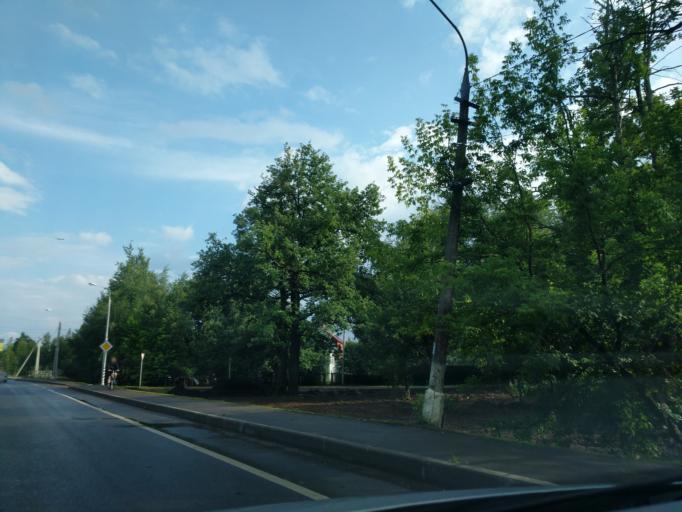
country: RU
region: Moskovskaya
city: Lobnya
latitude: 56.0099
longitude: 37.5073
